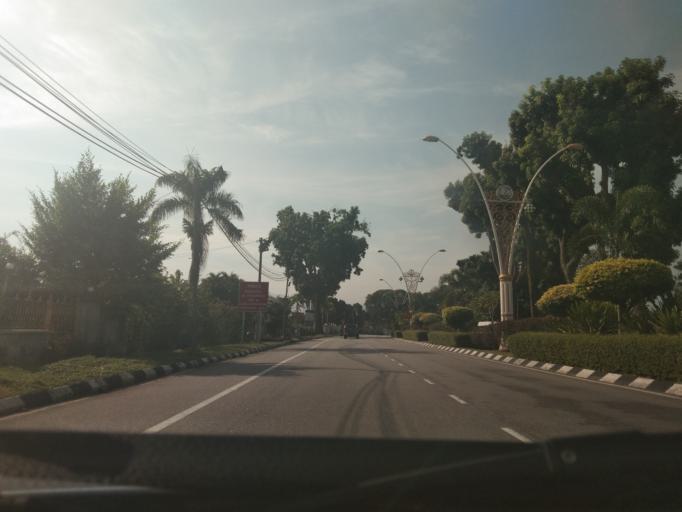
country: MY
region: Perak
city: Ipoh
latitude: 4.5881
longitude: 101.0967
